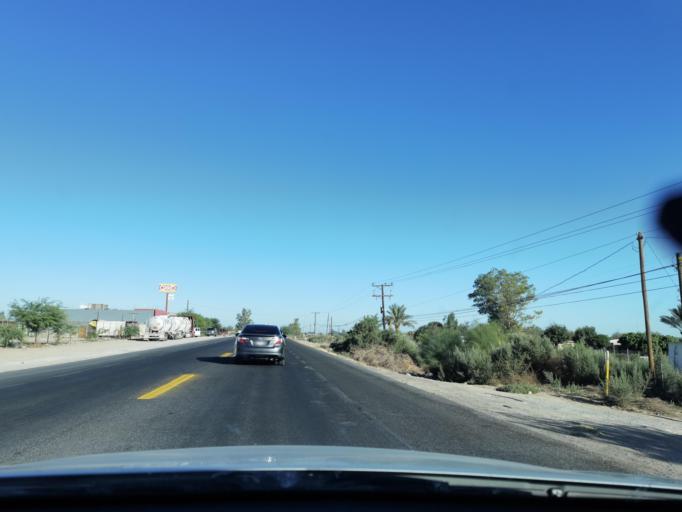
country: MX
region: Baja California
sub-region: Mexicali
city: Islas Agrarias Grupo A
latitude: 32.6449
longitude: -115.3177
